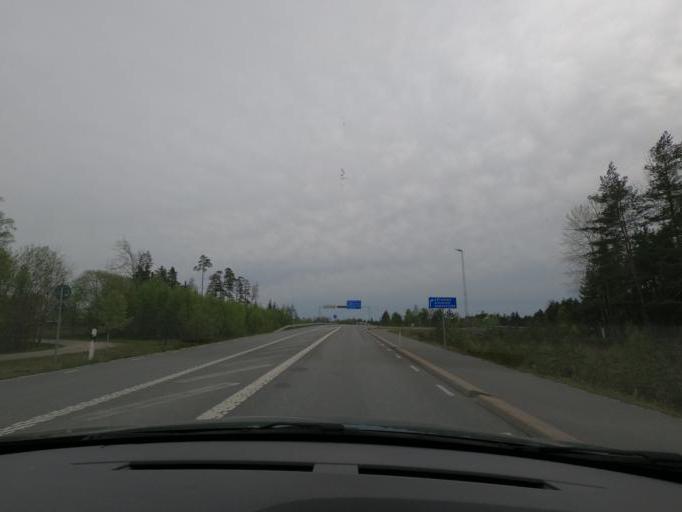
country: SE
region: Joenkoeping
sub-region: Varnamo Kommun
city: Bredaryd
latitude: 57.1825
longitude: 13.7496
